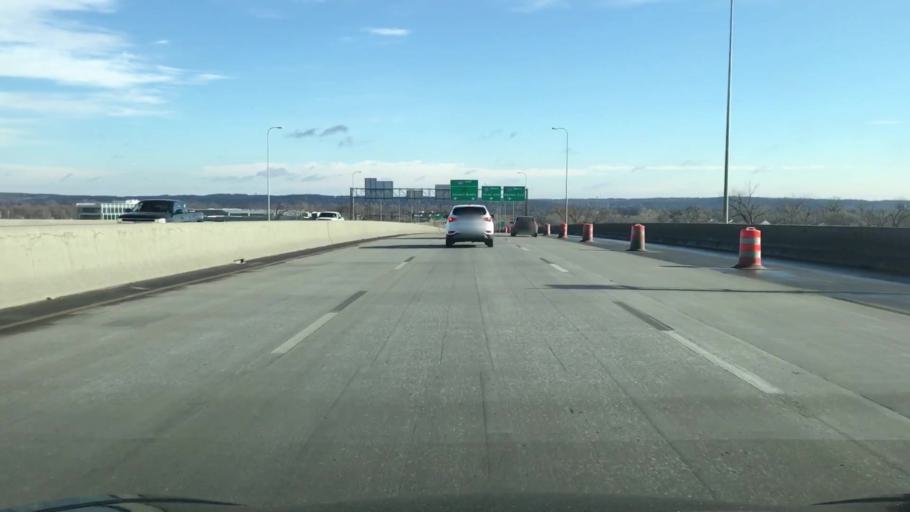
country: US
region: Nebraska
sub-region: Douglas County
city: Omaha
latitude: 41.2596
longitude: -95.9226
